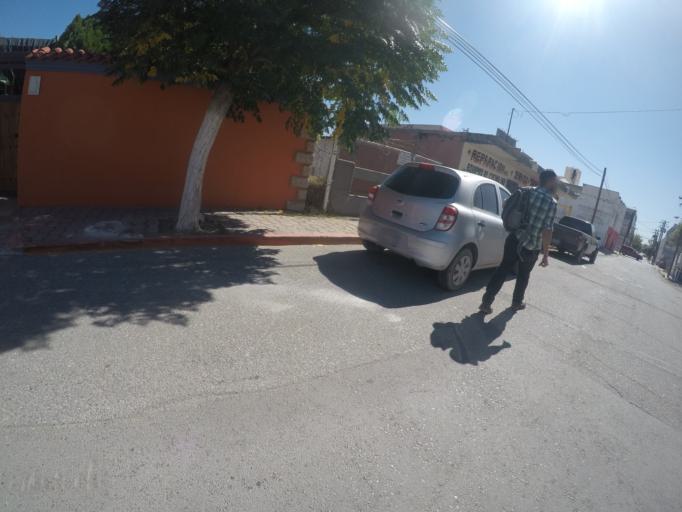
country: MX
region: Chihuahua
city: Ciudad Juarez
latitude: 31.7392
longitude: -106.4730
